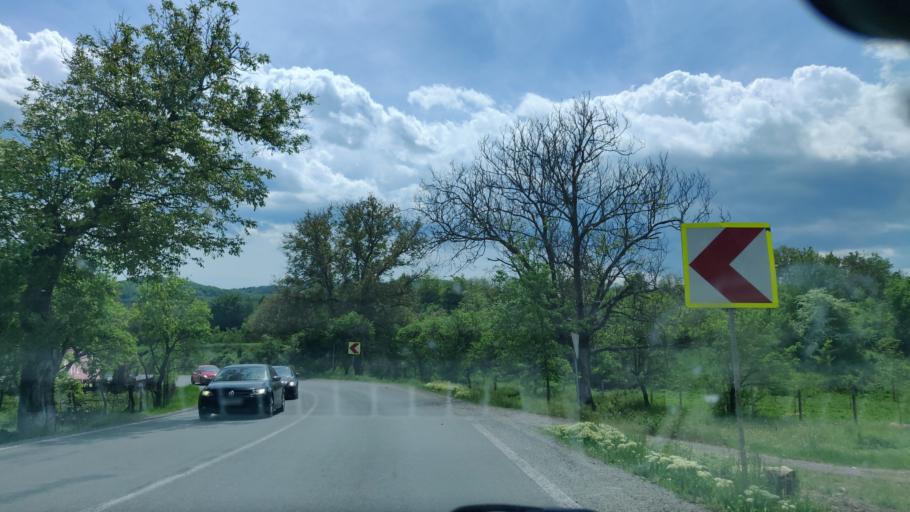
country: RO
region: Vrancea
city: Matacina
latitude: 45.8961
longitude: 26.8499
